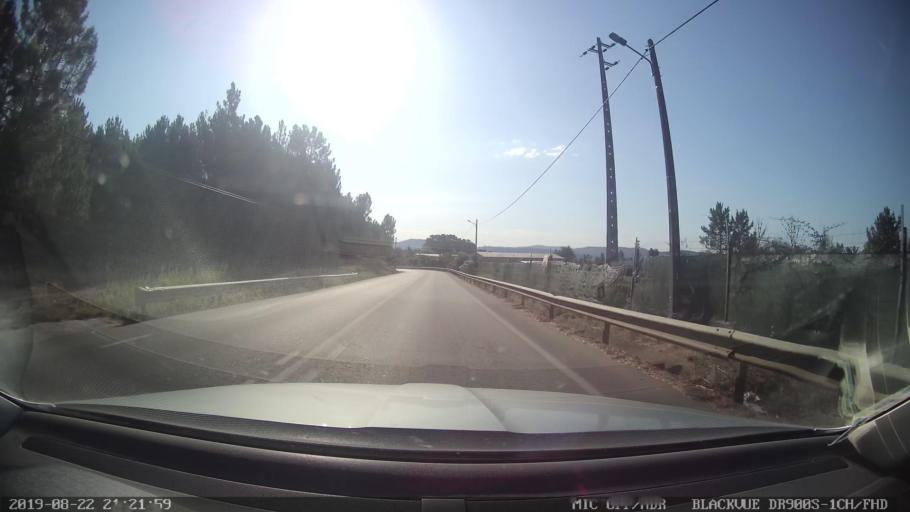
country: PT
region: Castelo Branco
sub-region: Serta
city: Serta
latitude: 39.8202
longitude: -8.1062
